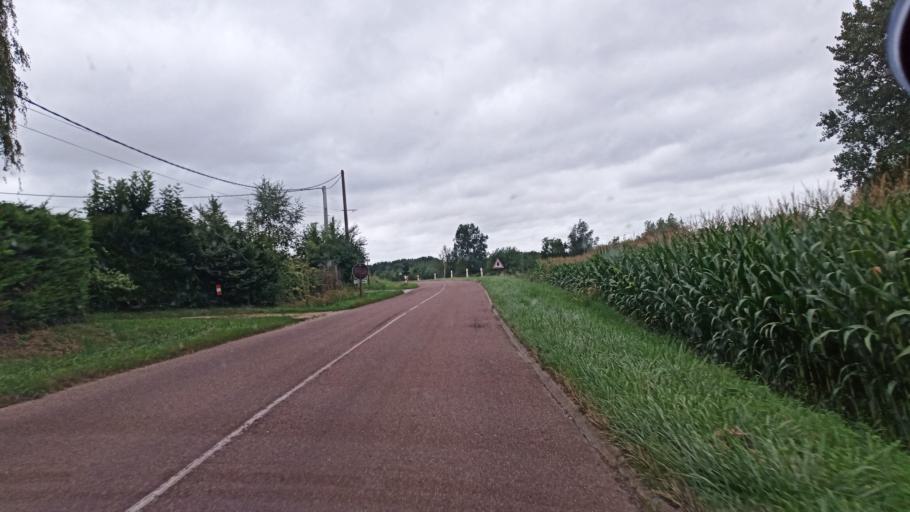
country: FR
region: Ile-de-France
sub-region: Departement de Seine-et-Marne
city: Voulx
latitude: 48.2690
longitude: 3.0005
